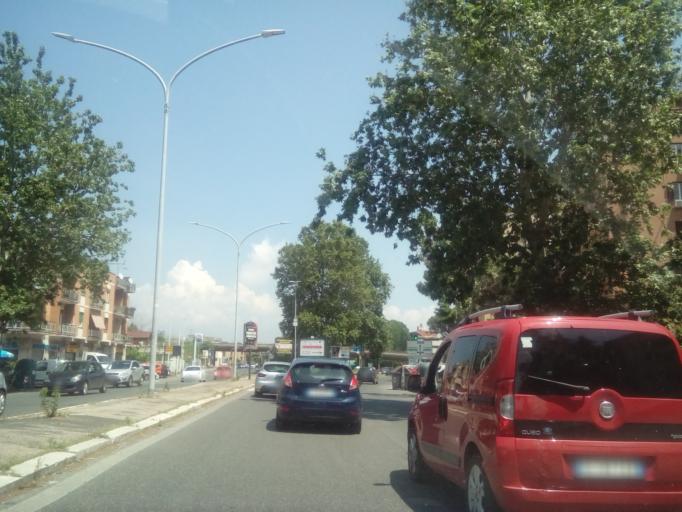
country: IT
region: Latium
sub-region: Citta metropolitana di Roma Capitale
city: Rome
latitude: 41.9114
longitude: 12.5511
